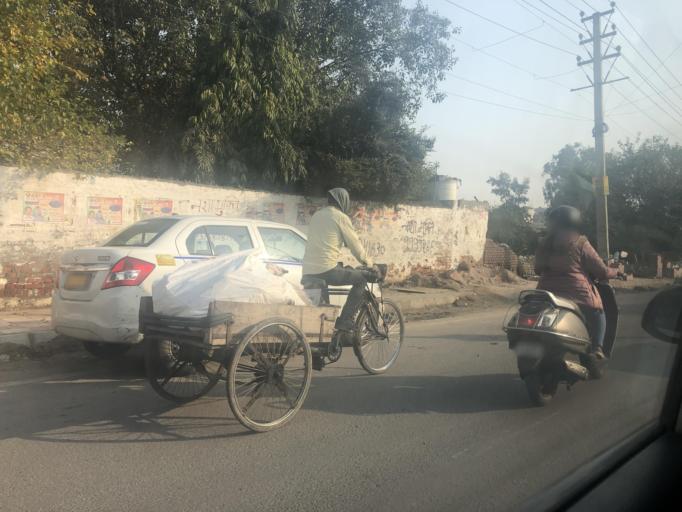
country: IN
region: Haryana
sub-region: Jhajjar
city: Bahadurgarh
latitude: 28.6178
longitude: 76.9753
